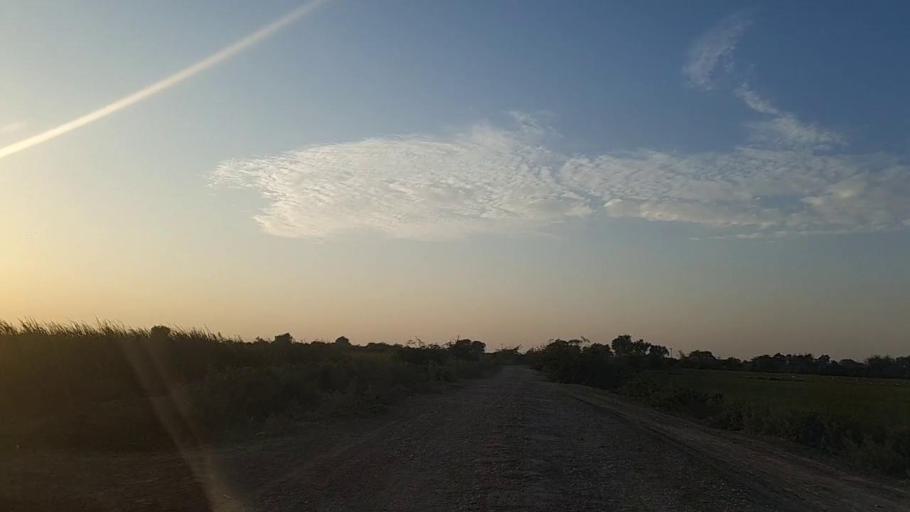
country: PK
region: Sindh
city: Chuhar Jamali
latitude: 24.4477
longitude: 68.1197
